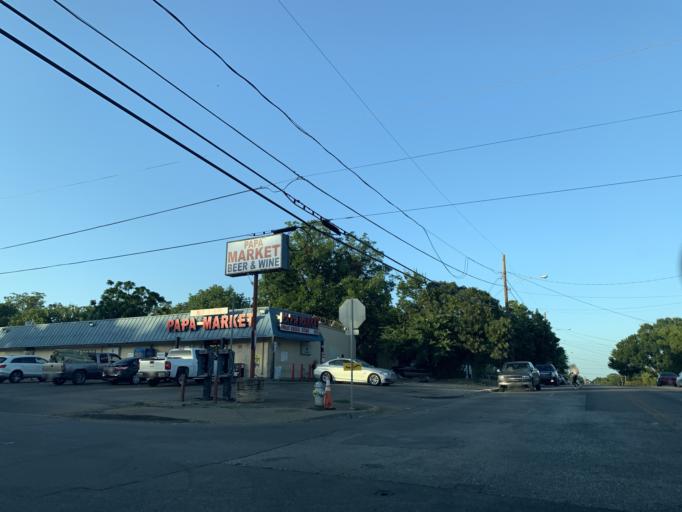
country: US
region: Texas
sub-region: Dallas County
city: Dallas
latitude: 32.7014
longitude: -96.8062
